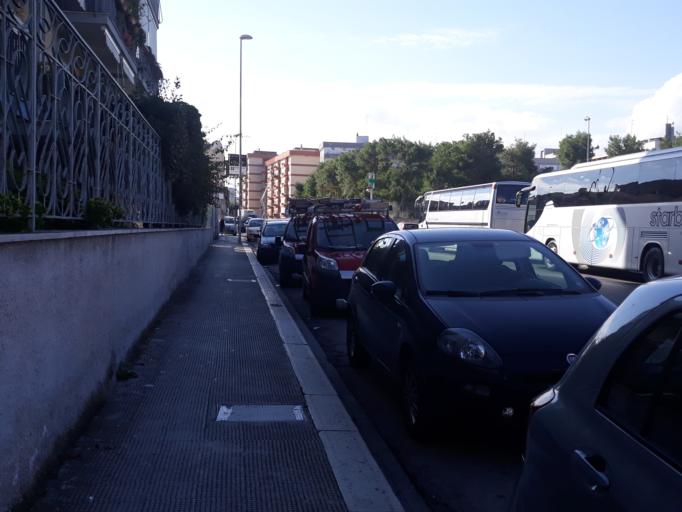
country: IT
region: Apulia
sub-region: Provincia di Bari
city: Bari
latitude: 41.1102
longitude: 16.8950
